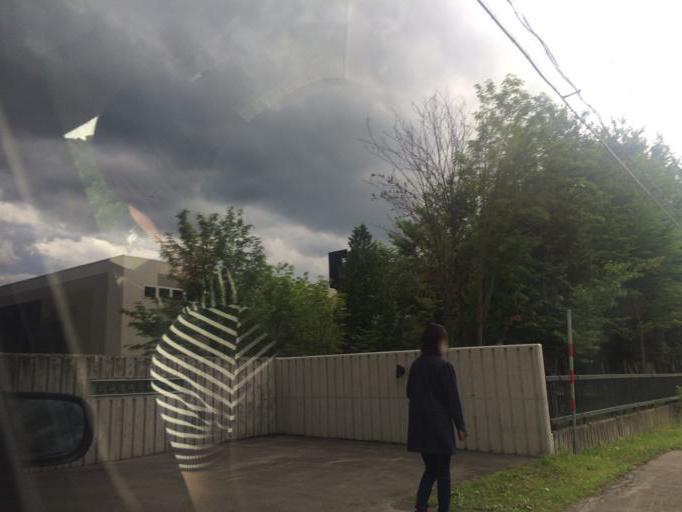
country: JP
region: Hokkaido
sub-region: Asahikawa-shi
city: Asahikawa
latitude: 43.7687
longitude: 142.2866
